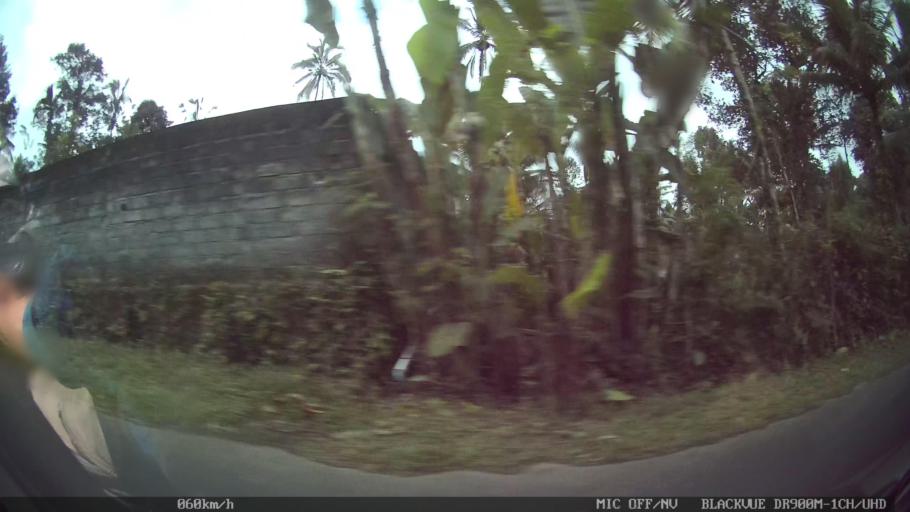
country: ID
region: Bali
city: Banjar Geriana Kangin
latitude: -8.4042
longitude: 115.4402
